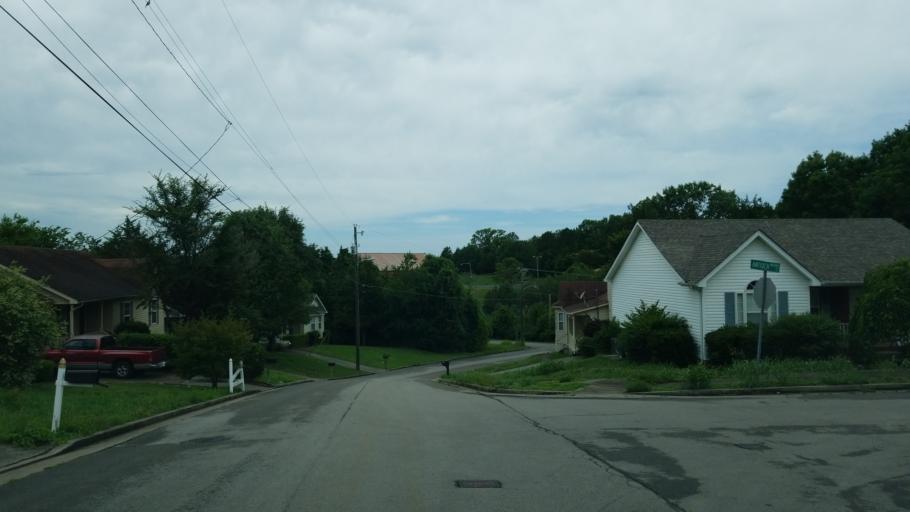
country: US
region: Tennessee
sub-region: Rutherford County
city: La Vergne
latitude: 36.0599
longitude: -86.6658
